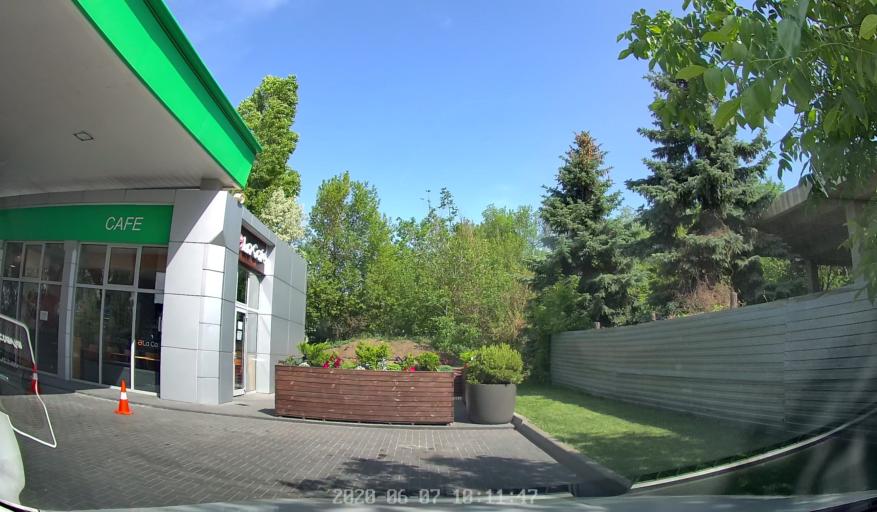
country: MD
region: Laloveni
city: Ialoveni
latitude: 46.9917
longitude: 28.7878
